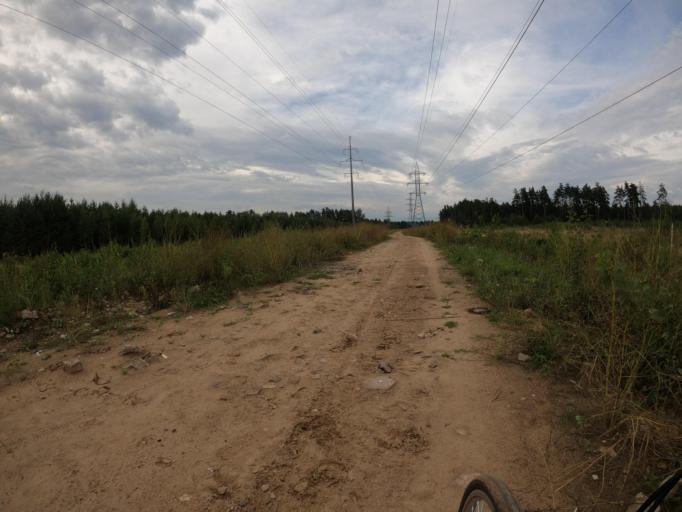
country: RU
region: Moskovskaya
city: Rodniki
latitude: 55.6769
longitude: 38.0858
